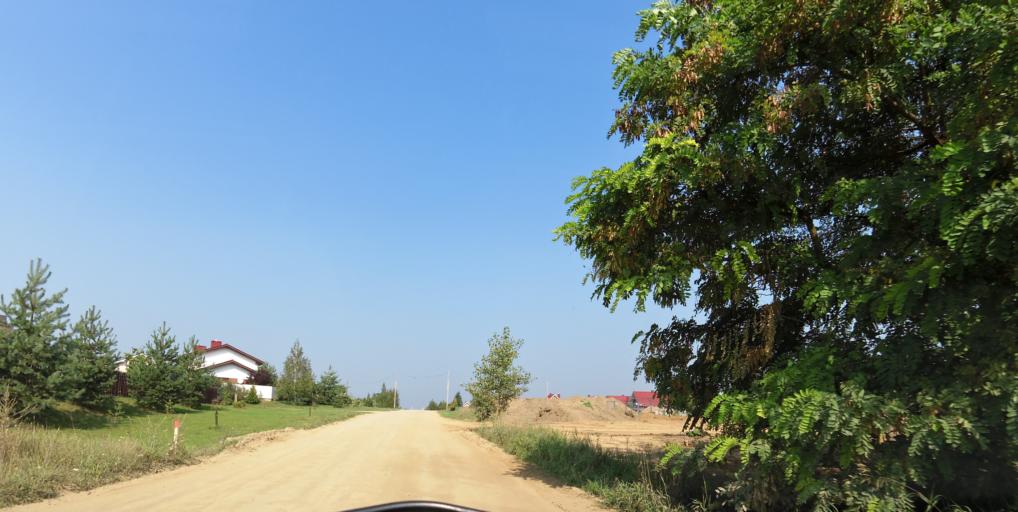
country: LT
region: Vilnius County
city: Pasilaiciai
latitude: 54.7281
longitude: 25.2059
